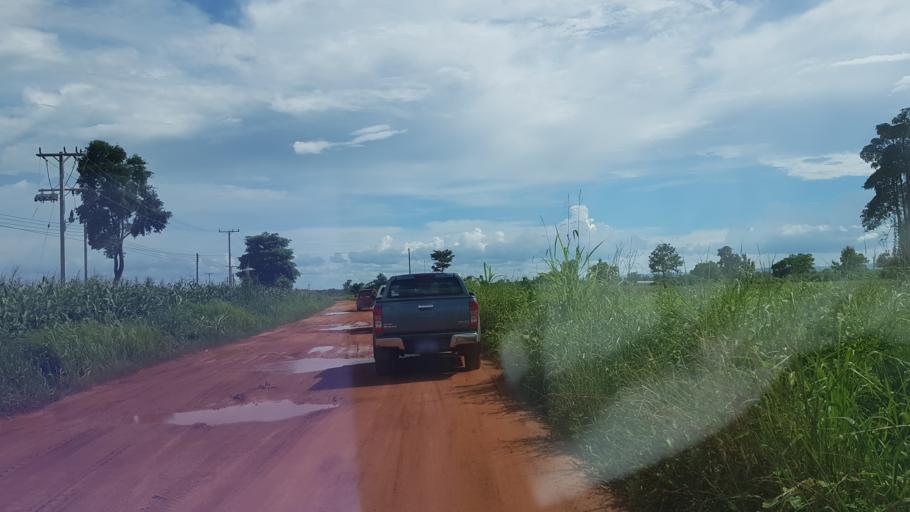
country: LA
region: Vientiane
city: Vientiane
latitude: 18.2137
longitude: 102.5668
